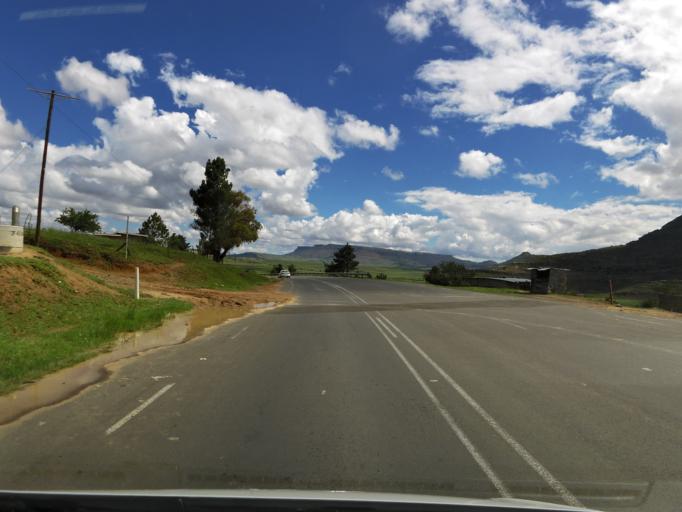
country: LS
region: Maseru
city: Maseru
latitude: -29.5093
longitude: 27.5238
